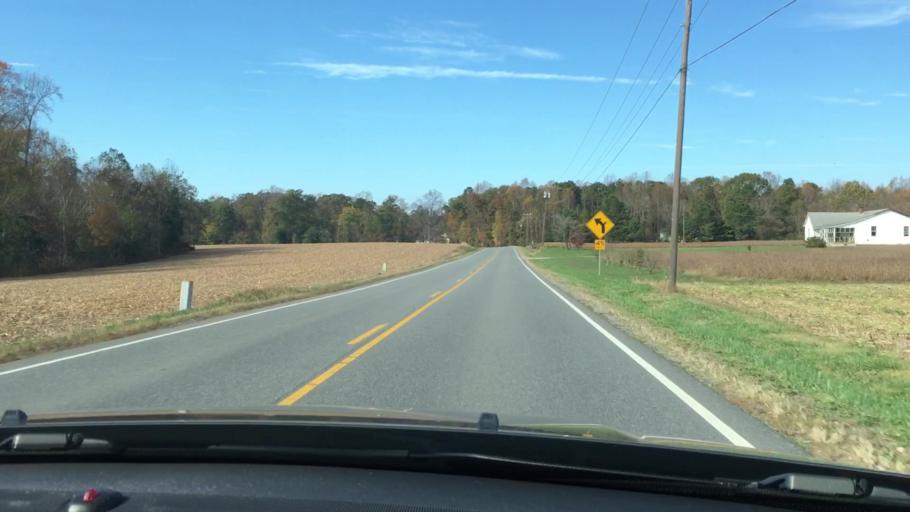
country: US
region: Virginia
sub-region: King William County
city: West Point
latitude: 37.5884
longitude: -76.8560
